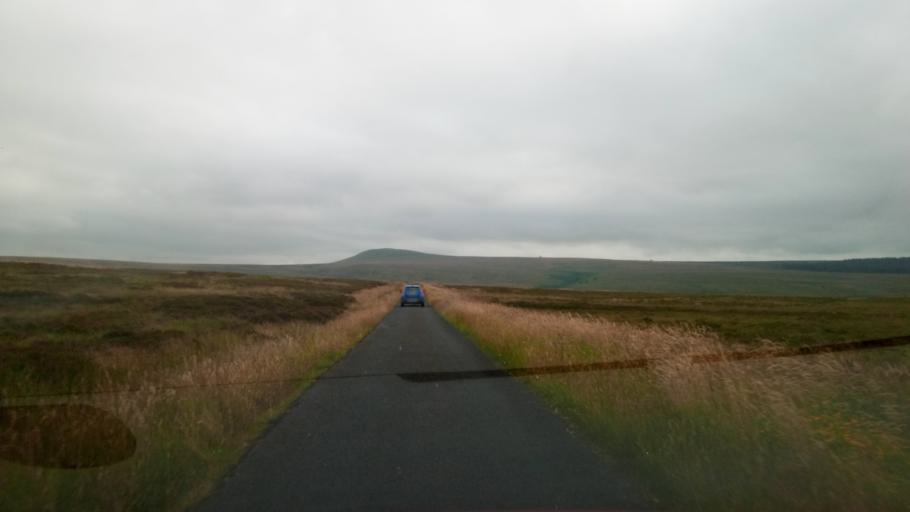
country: GB
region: Scotland
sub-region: Dumfries and Galloway
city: Langholm
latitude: 55.1693
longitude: -2.9476
